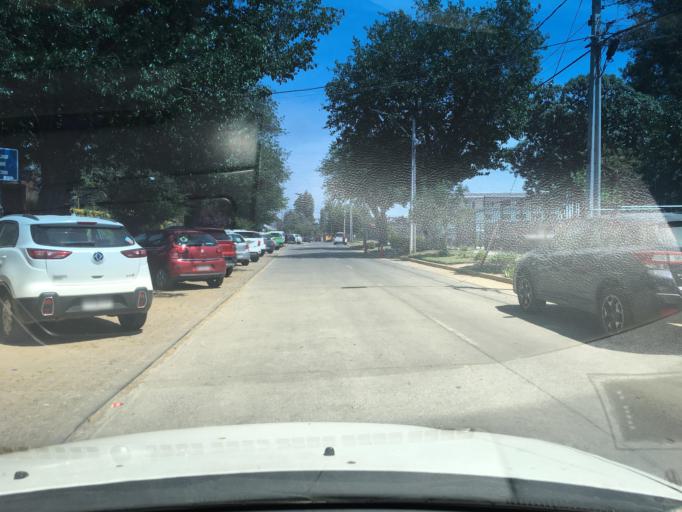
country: CL
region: Santiago Metropolitan
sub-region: Provincia de Santiago
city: Villa Presidente Frei, Nunoa, Santiago, Chile
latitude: -33.4666
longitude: -70.5714
